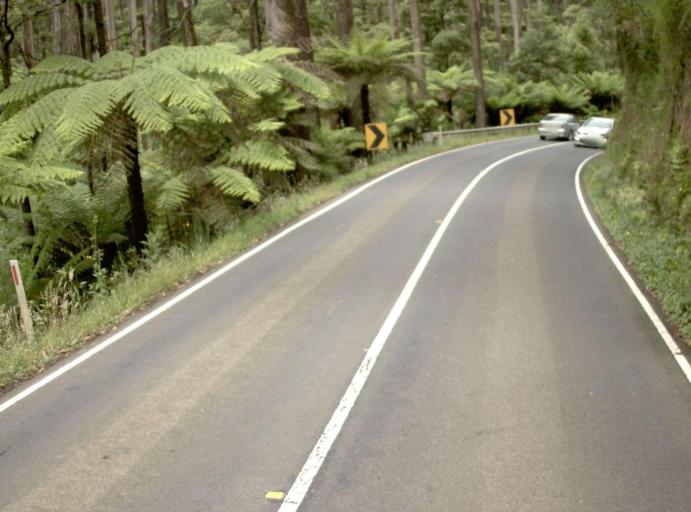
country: AU
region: Victoria
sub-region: Yarra Ranges
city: Healesville
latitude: -37.5946
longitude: 145.6400
